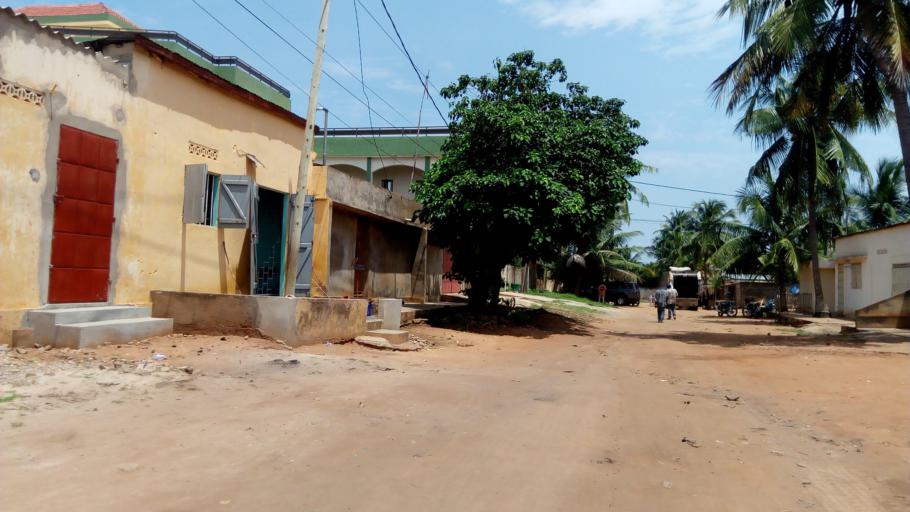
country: TG
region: Maritime
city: Lome
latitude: 6.1826
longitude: 1.1747
